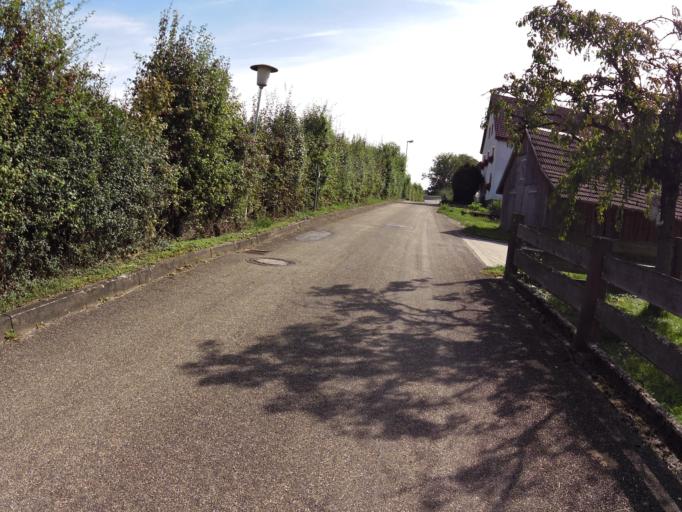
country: DE
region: Baden-Wuerttemberg
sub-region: Freiburg Region
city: Muhlheim am Bach
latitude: 48.3901
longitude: 8.6726
